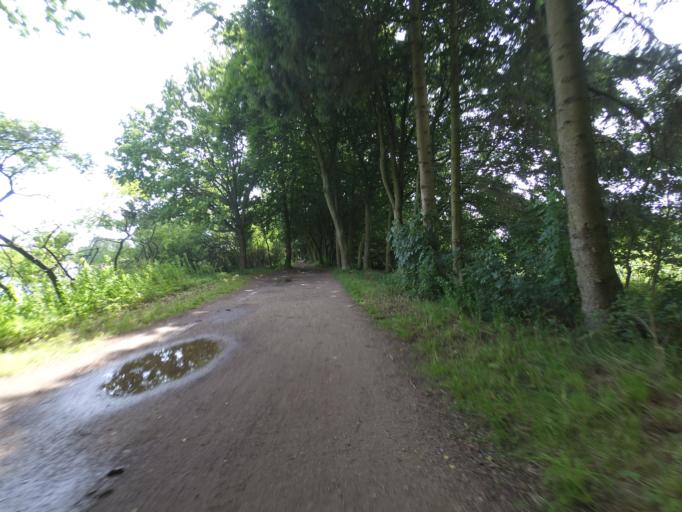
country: DE
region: Schleswig-Holstein
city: Barsbuettel
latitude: 53.5637
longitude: 10.1384
